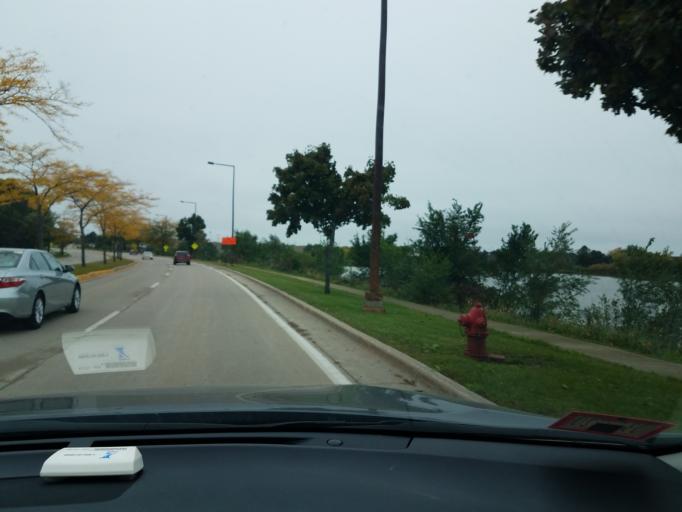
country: US
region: Illinois
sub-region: Cook County
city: Wheeling
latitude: 42.1688
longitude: -87.9296
